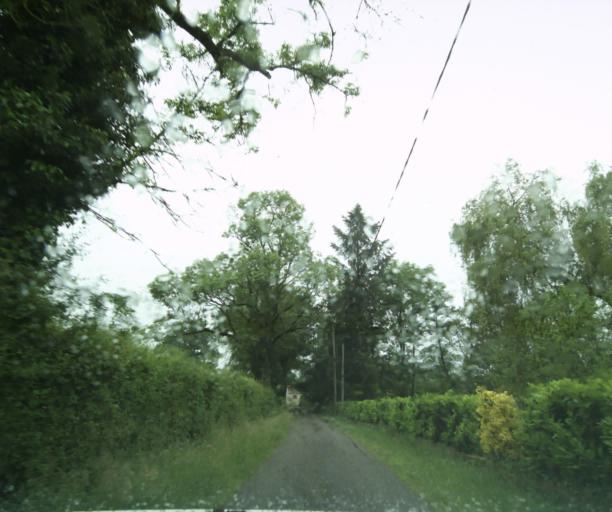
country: FR
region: Bourgogne
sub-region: Departement de Saone-et-Loire
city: Charolles
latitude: 46.3796
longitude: 4.3559
